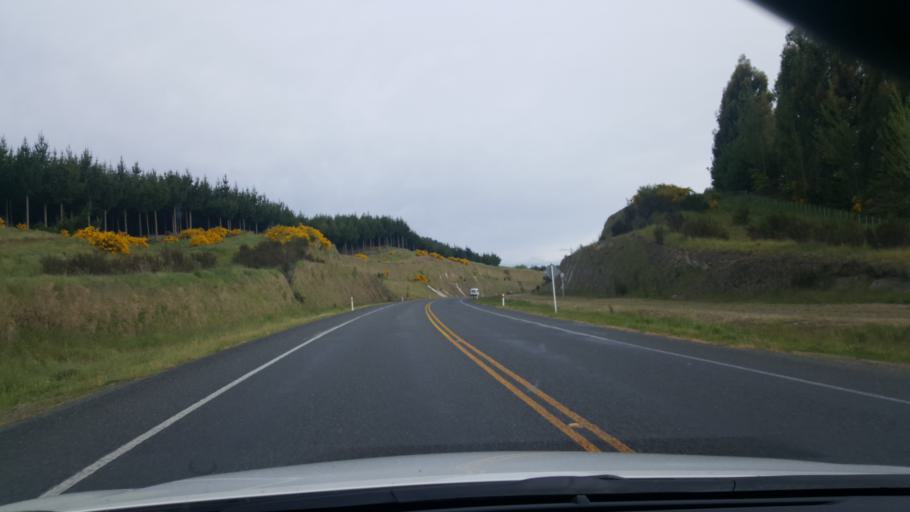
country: NZ
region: Waikato
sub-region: Taupo District
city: Taupo
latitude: -38.6716
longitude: 176.1135
